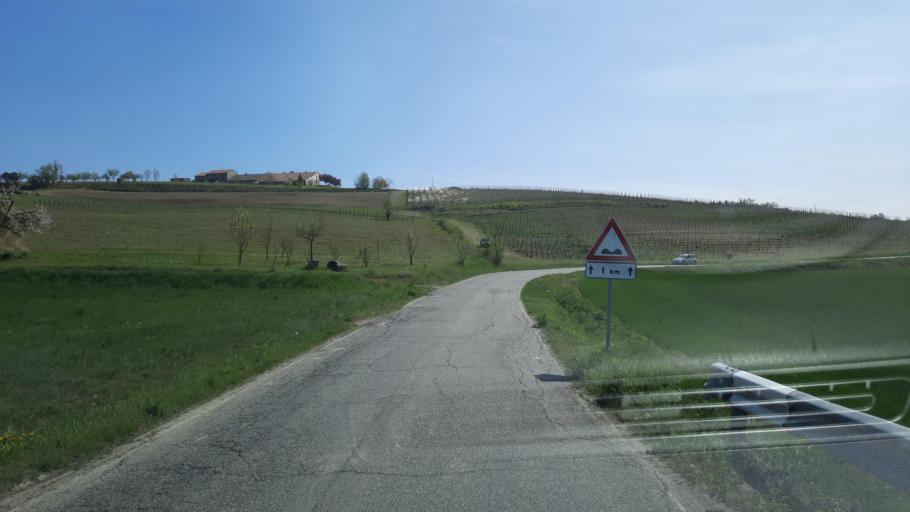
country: IT
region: Piedmont
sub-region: Provincia di Alessandria
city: Sala Monferrato
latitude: 45.0809
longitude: 8.3661
